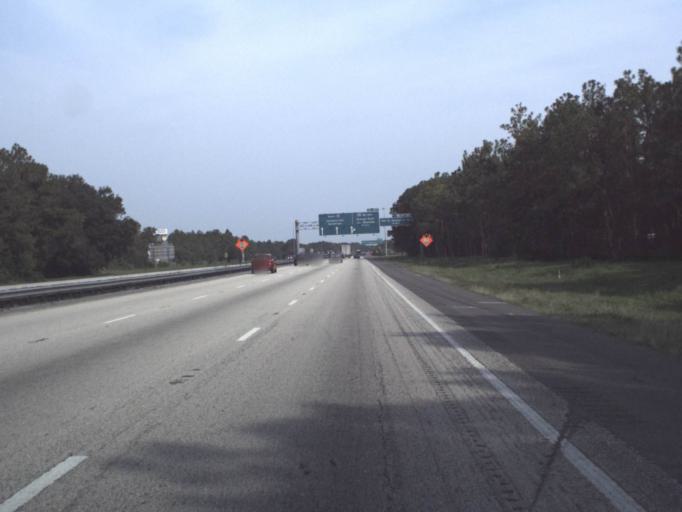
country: US
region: Florida
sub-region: Saint Johns County
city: Fruit Cove
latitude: 30.1330
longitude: -81.5322
